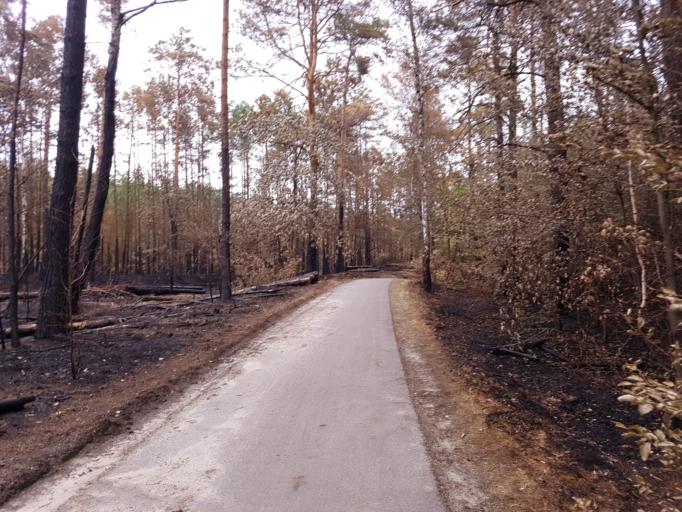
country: DE
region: Brandenburg
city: Finsterwalde
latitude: 51.6293
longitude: 13.6724
